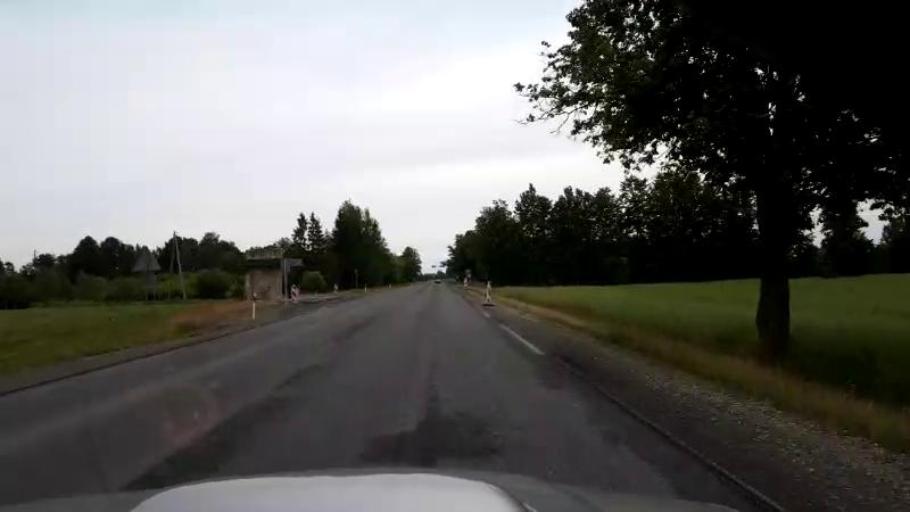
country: LV
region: Bauskas Rajons
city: Bauska
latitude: 56.3201
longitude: 24.3198
